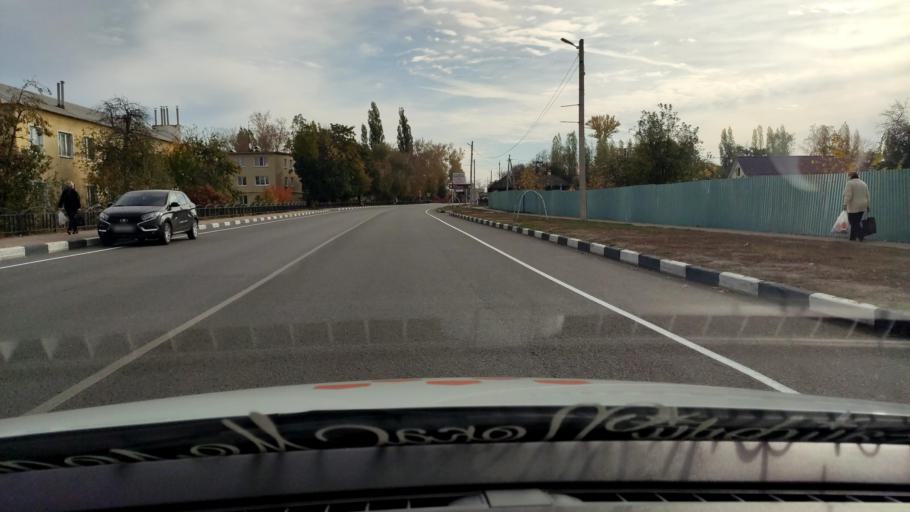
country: RU
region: Voronezj
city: Ramon'
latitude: 51.9099
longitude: 39.3331
